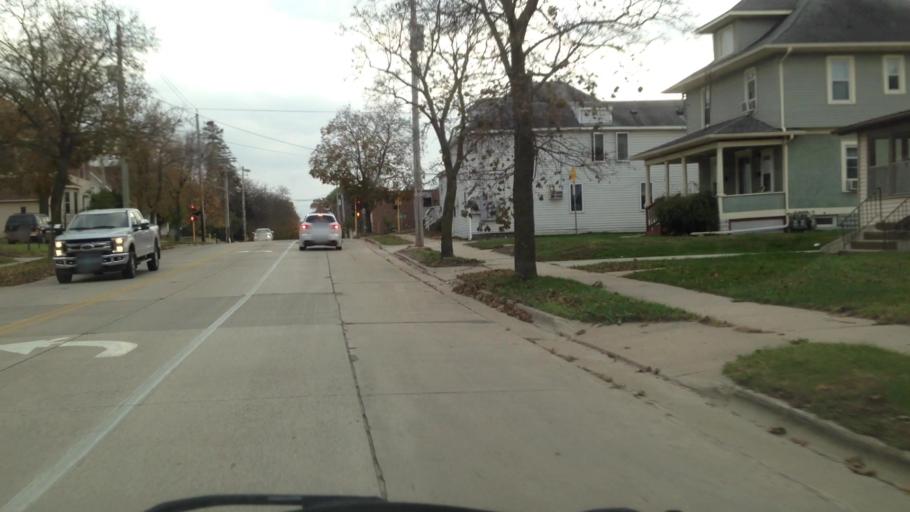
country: US
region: Minnesota
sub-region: Olmsted County
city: Rochester
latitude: 44.0244
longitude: -92.4489
